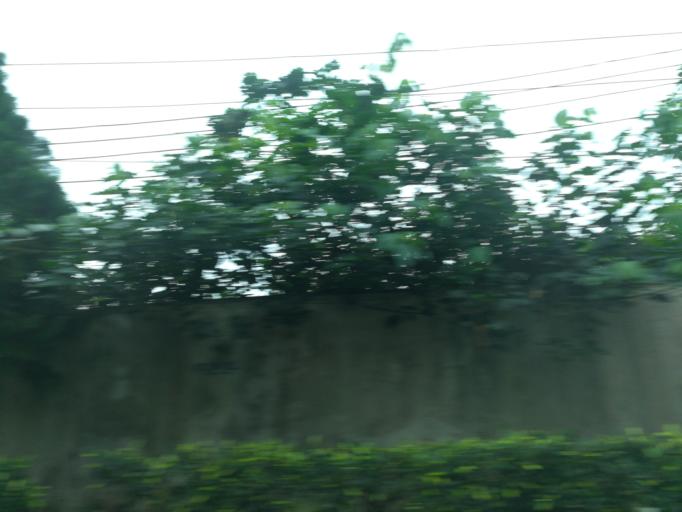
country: NG
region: Rivers
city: Port Harcourt
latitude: 4.8354
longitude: 7.0201
